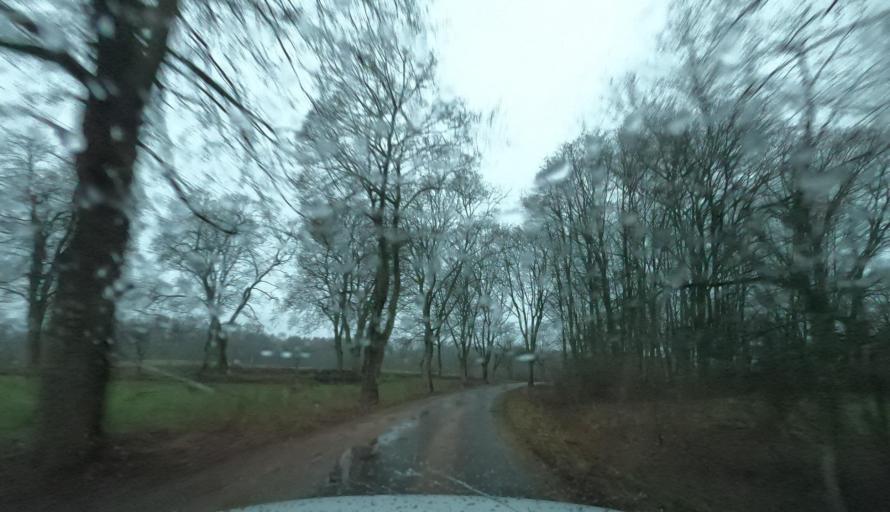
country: PL
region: West Pomeranian Voivodeship
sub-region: Powiat szczecinecki
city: Borne Sulinowo
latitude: 53.6942
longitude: 16.4945
